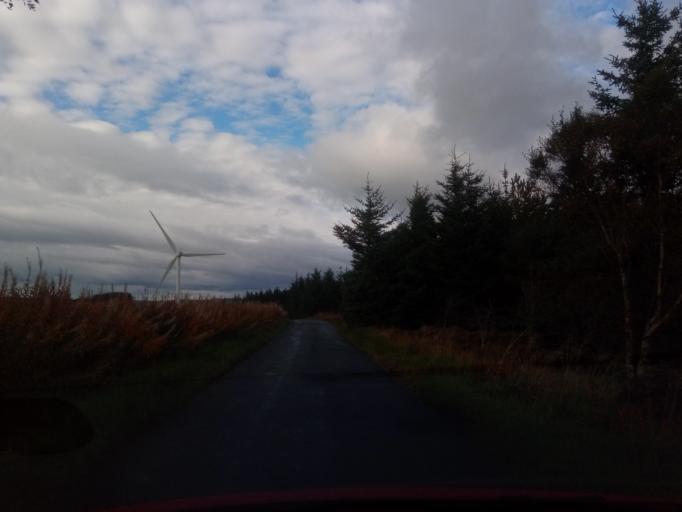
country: GB
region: Scotland
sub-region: The Scottish Borders
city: Galashiels
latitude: 55.6874
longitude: -2.8505
